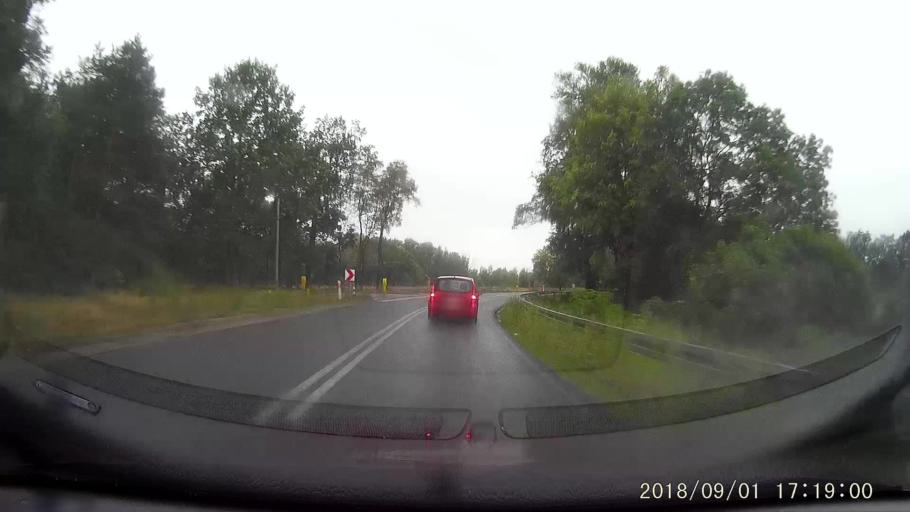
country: PL
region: Lubusz
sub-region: Powiat zielonogorski
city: Nowogrod Bobrzanski
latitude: 51.7342
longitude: 15.2745
